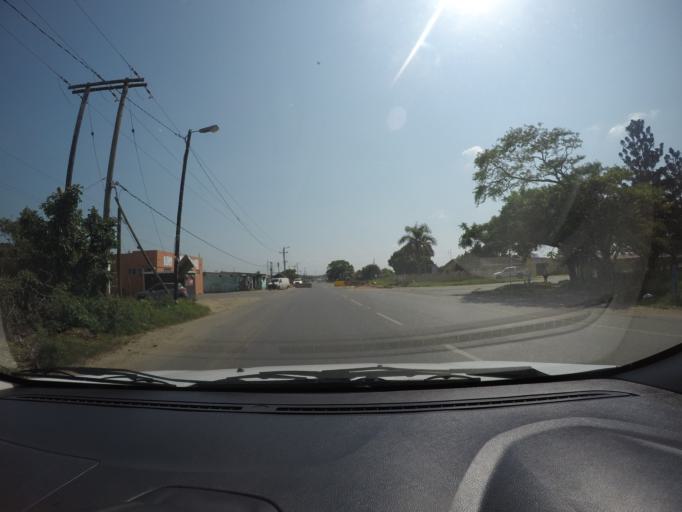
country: ZA
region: KwaZulu-Natal
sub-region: uThungulu District Municipality
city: eSikhawini
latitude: -28.8760
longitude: 31.8949
